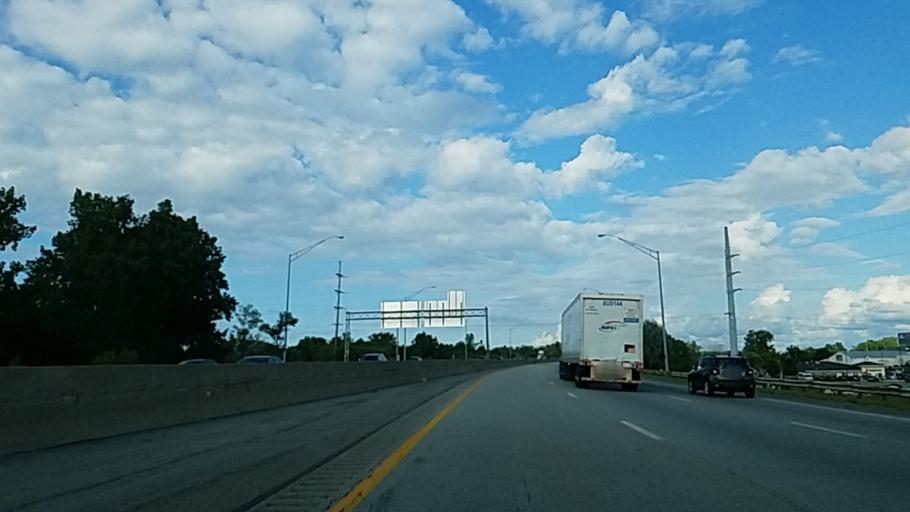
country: US
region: Ohio
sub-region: Lorain County
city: North Ridgeville
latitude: 41.3863
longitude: -81.9804
